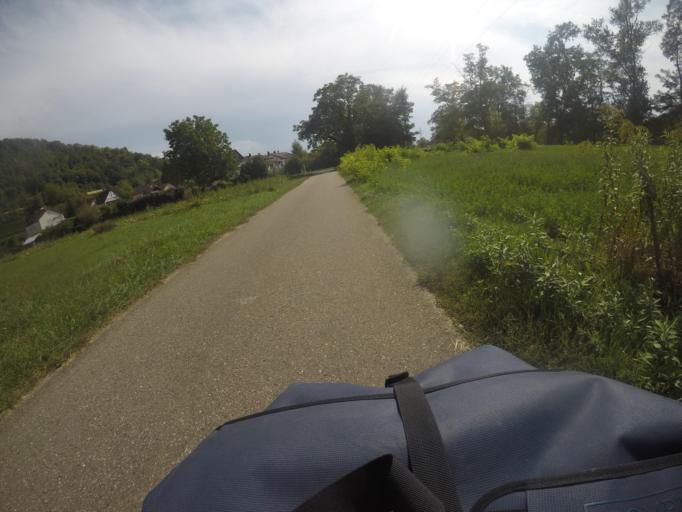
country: FR
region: Alsace
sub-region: Departement du Haut-Rhin
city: Kembs
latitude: 47.6919
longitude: 7.5231
